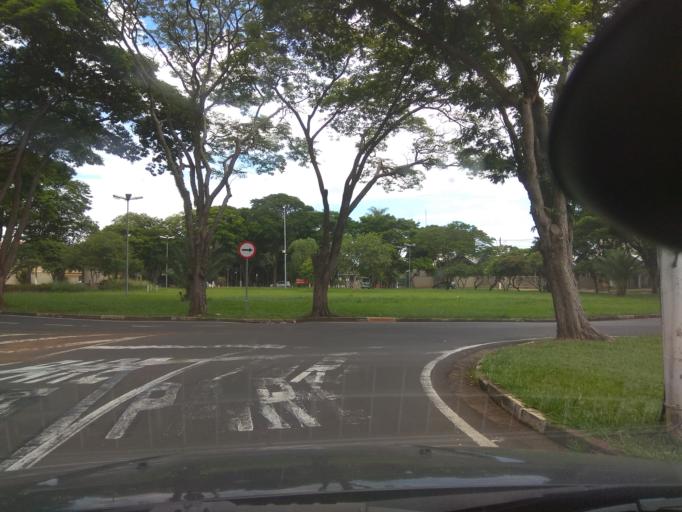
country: BR
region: Sao Paulo
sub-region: Campinas
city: Campinas
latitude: -22.8188
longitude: -47.0724
